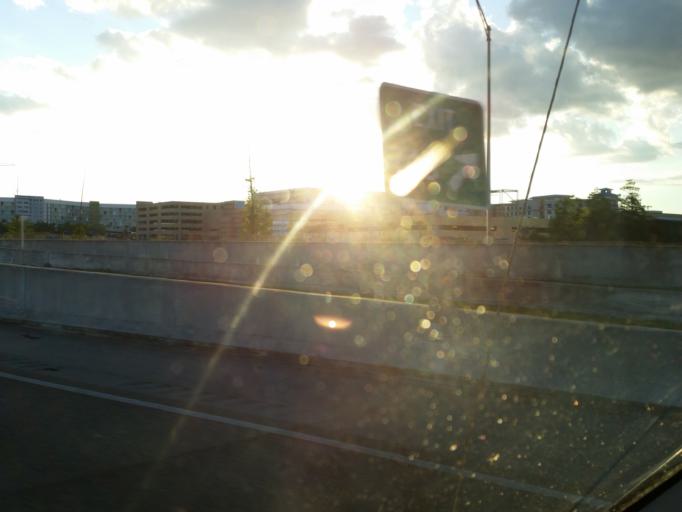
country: US
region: Florida
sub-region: Orange County
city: Tangelo Park
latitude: 28.4651
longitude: -81.4662
